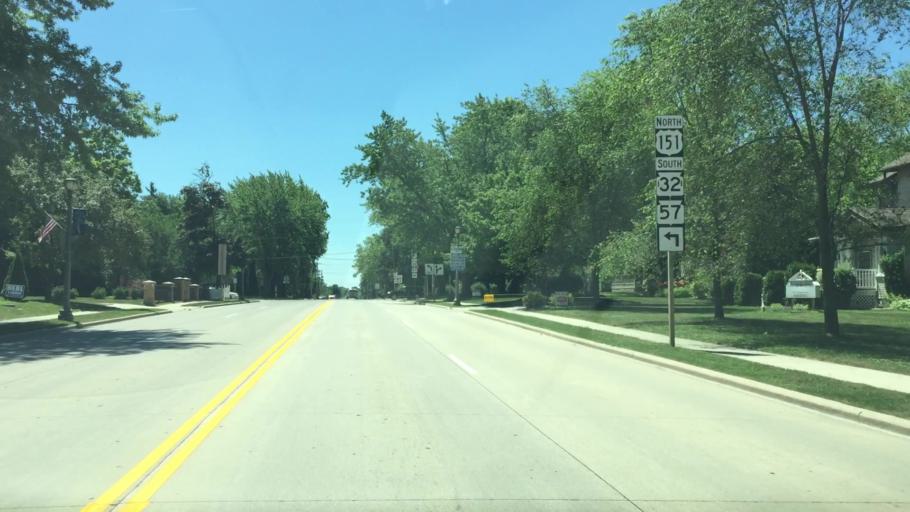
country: US
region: Wisconsin
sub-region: Calumet County
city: Chilton
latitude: 44.0251
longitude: -88.1628
